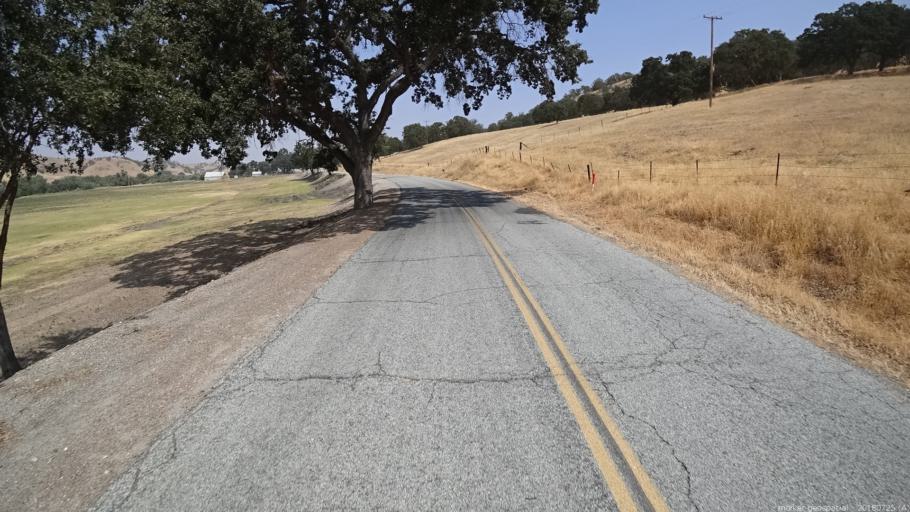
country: US
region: California
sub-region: San Luis Obispo County
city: San Miguel
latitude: 35.8056
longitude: -120.6741
